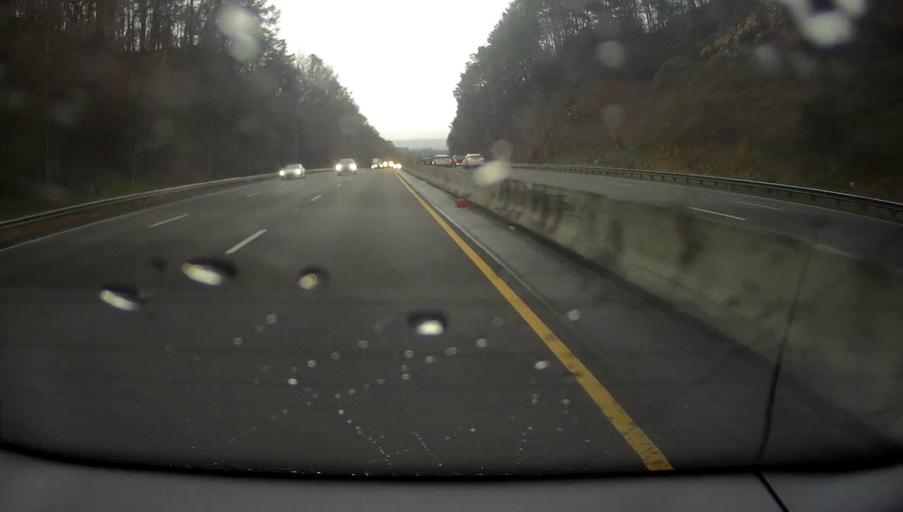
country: US
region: Alabama
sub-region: Blount County
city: Smoke Rise
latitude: 33.8968
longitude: -86.8577
